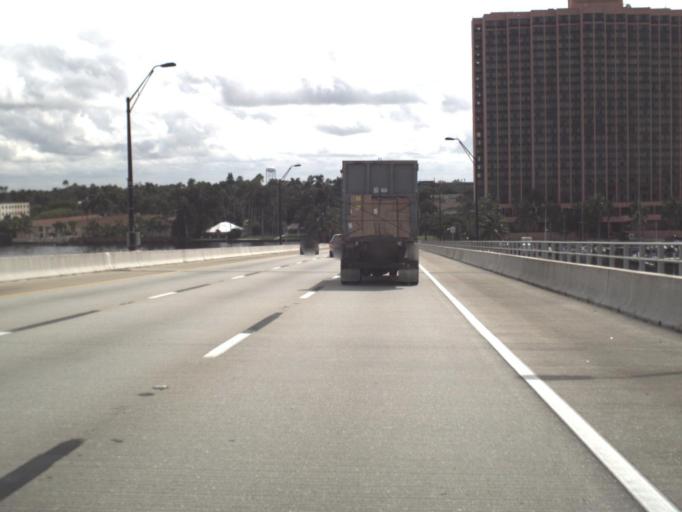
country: US
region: Florida
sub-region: Lee County
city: North Fort Myers
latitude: 26.6501
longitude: -81.8686
